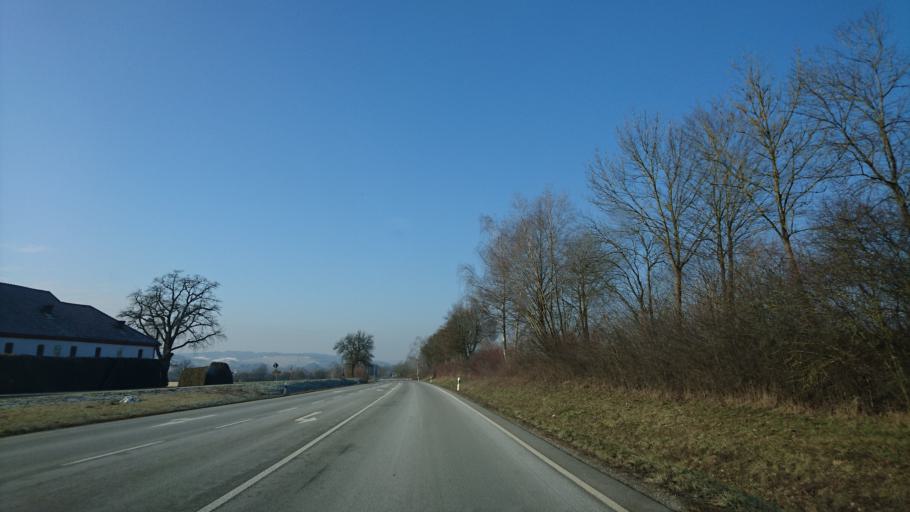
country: DE
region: Bavaria
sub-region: Lower Bavaria
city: Bayerbach
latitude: 48.4314
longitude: 13.1377
